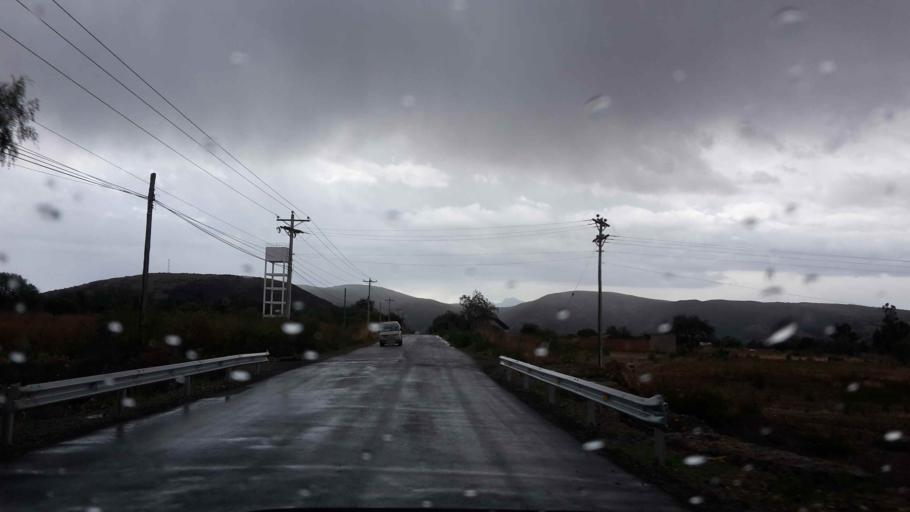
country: BO
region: Cochabamba
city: Tarata
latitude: -17.5579
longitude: -66.0857
